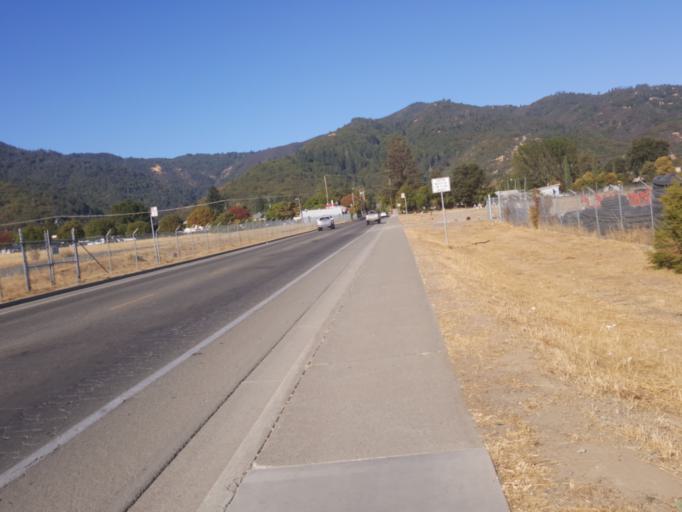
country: US
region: California
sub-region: Mendocino County
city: Ukiah
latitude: 39.1342
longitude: -123.2019
